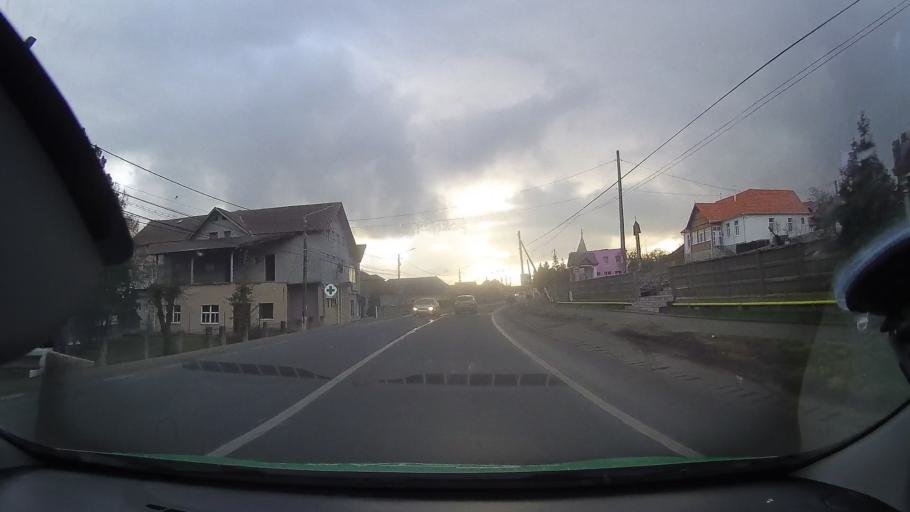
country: RO
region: Cluj
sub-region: Comuna Luna
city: Luncani
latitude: 46.5020
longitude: 23.9208
